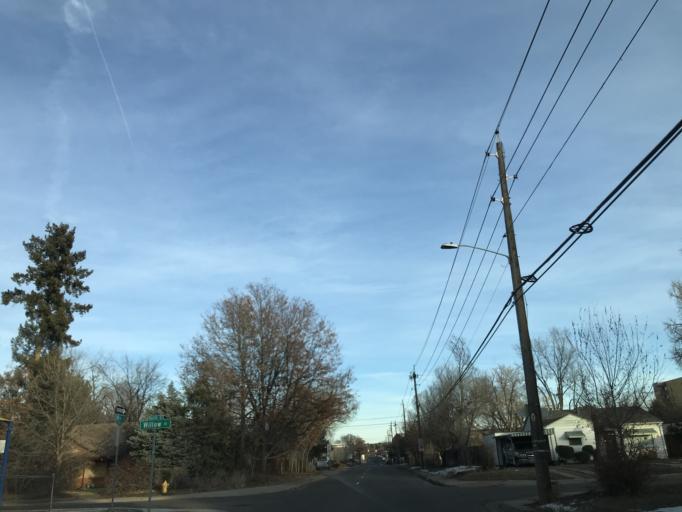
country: US
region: Colorado
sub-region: Arapahoe County
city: Glendale
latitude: 39.7387
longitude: -104.8886
